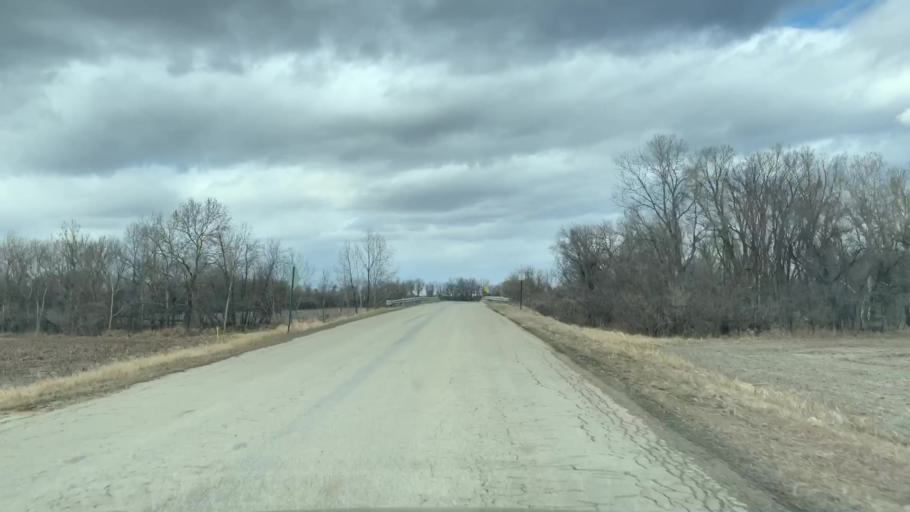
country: US
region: Kansas
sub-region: Allen County
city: Humboldt
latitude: 37.8034
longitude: -95.4711
